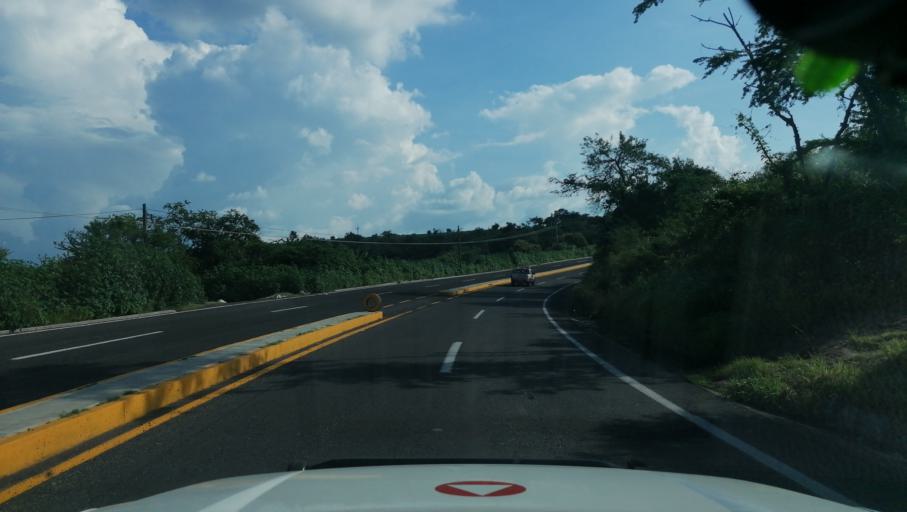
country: MX
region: Morelos
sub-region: Ayala
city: Abelardo L. Rodriguez
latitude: 18.7032
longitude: -98.9912
